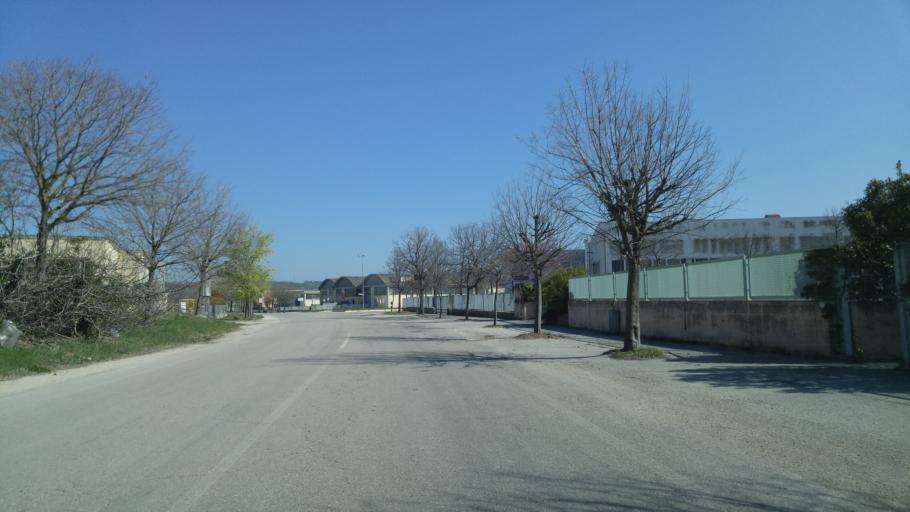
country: IT
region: The Marches
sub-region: Provincia di Pesaro e Urbino
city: Bellocchi
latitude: 43.7875
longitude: 13.0022
